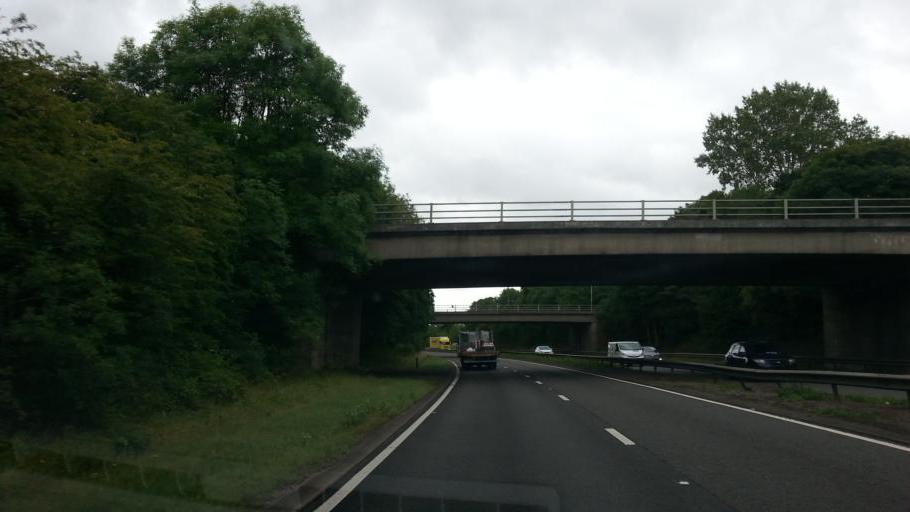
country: GB
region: England
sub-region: Warwickshire
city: Warwick
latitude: 52.2909
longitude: -1.6090
